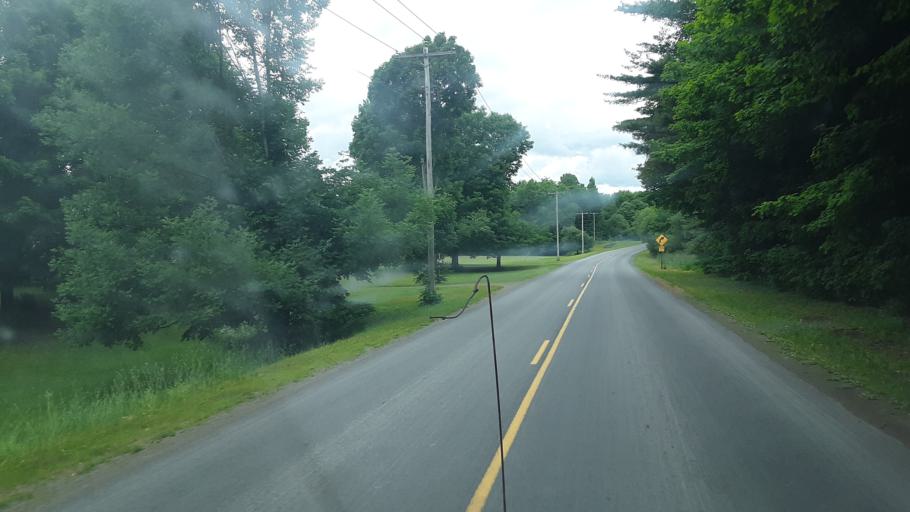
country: US
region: New York
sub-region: Oneida County
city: Rome
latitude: 43.3910
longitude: -75.5519
